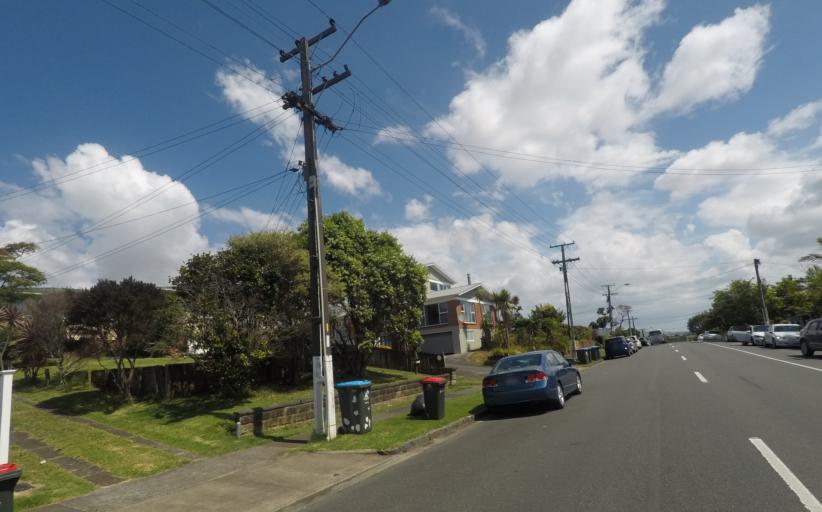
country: NZ
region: Auckland
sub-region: Auckland
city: Tamaki
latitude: -36.8950
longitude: 174.8105
